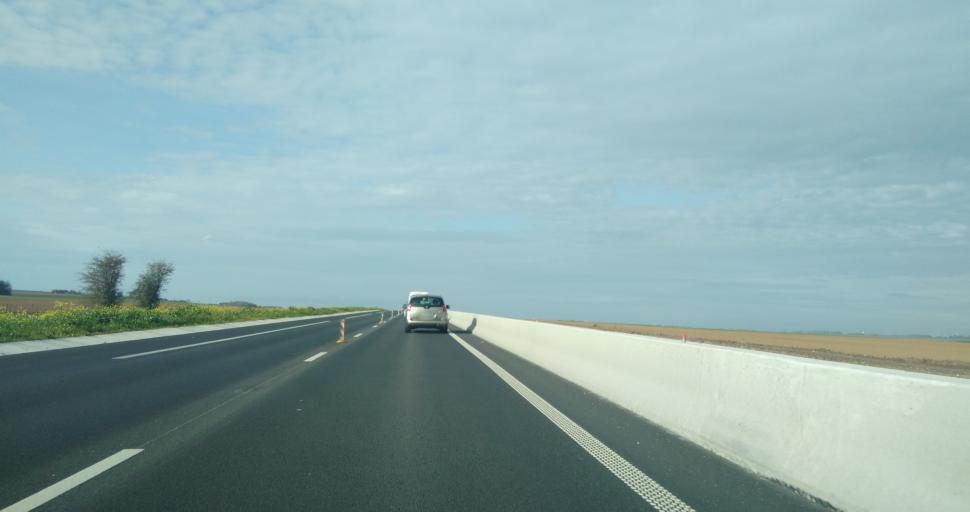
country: FR
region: Nord-Pas-de-Calais
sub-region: Departement du Pas-de-Calais
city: Aubigny-en-Artois
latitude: 50.3340
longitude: 2.6319
